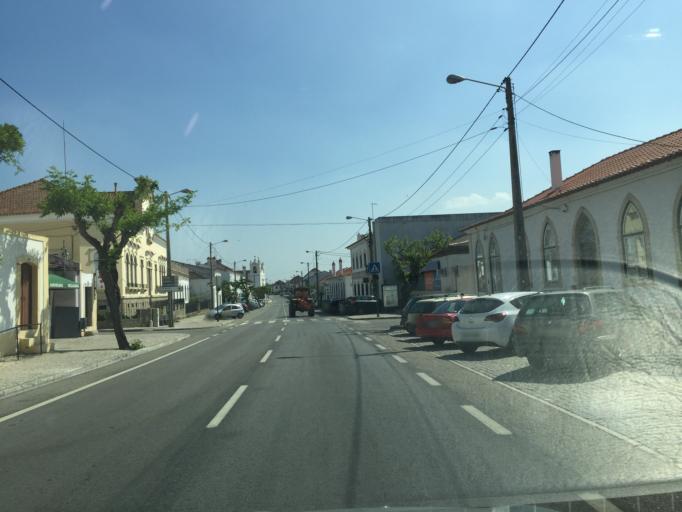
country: PT
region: Santarem
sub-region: Golega
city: Golega
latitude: 39.3577
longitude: -8.4827
